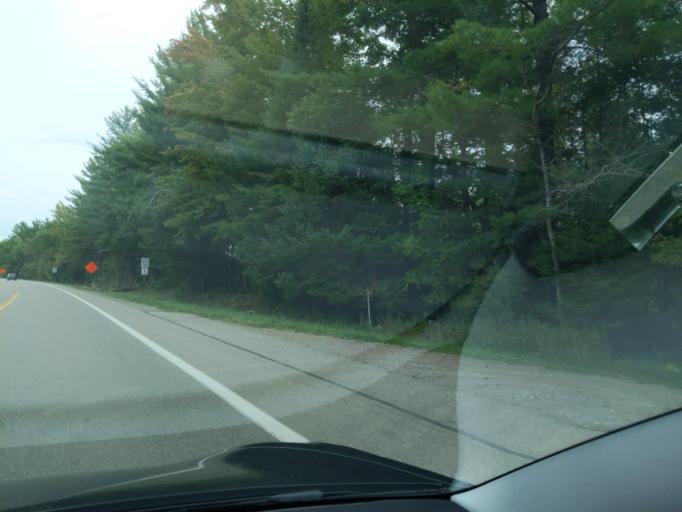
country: US
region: Michigan
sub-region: Clare County
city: Clare
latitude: 43.8373
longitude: -84.8794
